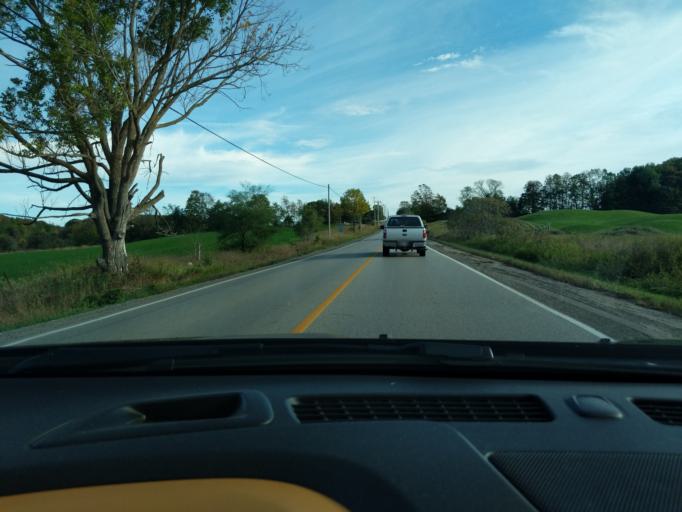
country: CA
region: Ontario
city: Barrie
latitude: 44.4227
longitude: -79.7607
